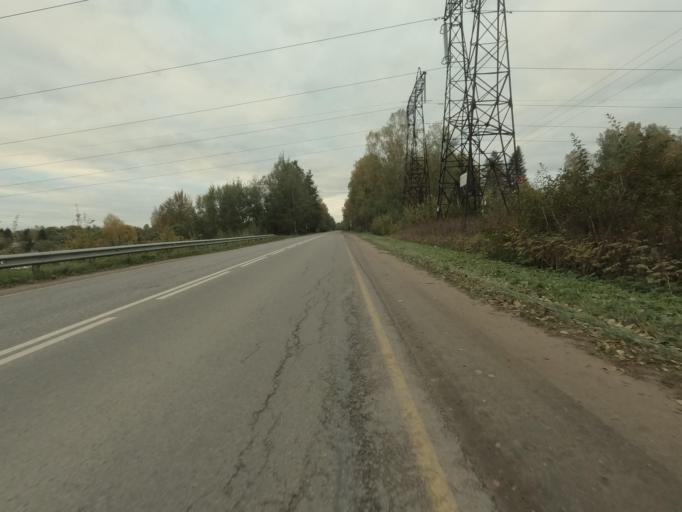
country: RU
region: Leningrad
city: Pavlovo
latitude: 59.7805
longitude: 30.9716
